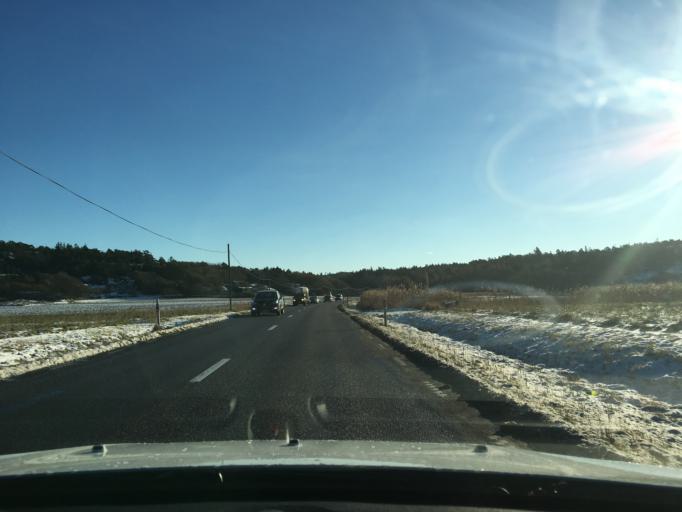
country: SE
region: Vaestra Goetaland
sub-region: Tjorns Kommun
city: Myggenas
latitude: 58.1040
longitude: 11.7051
